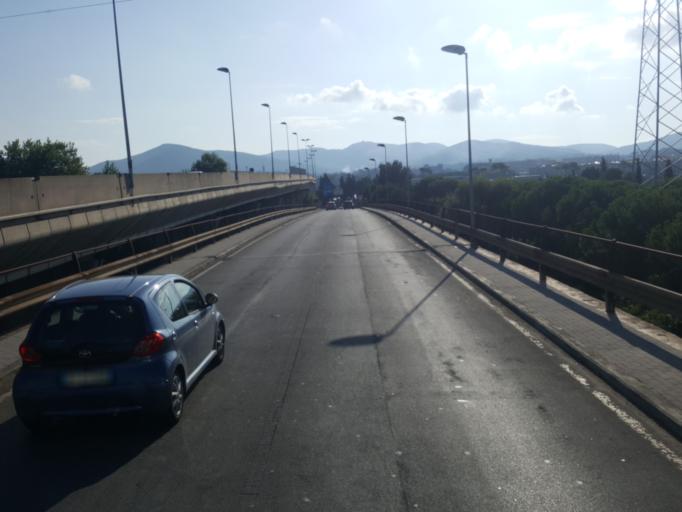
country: IT
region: Tuscany
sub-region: Provincia di Livorno
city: Livorno
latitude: 43.5317
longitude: 10.3317
